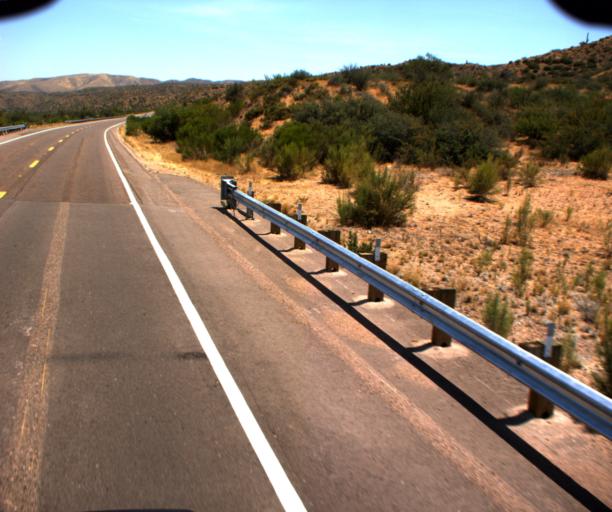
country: US
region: Arizona
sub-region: Gila County
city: Tonto Basin
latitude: 33.7742
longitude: -111.2611
